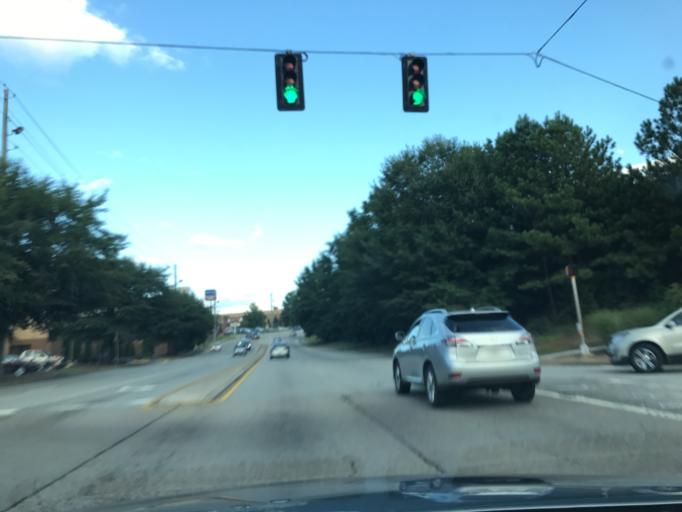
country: US
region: Georgia
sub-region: Douglas County
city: Douglasville
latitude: 33.7307
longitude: -84.7416
